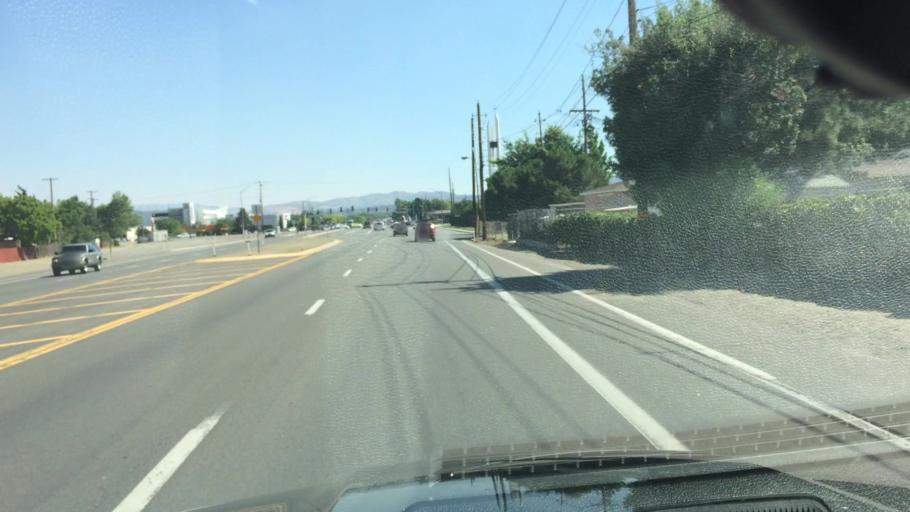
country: US
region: Nevada
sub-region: Washoe County
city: Reno
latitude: 39.5083
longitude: -119.7893
